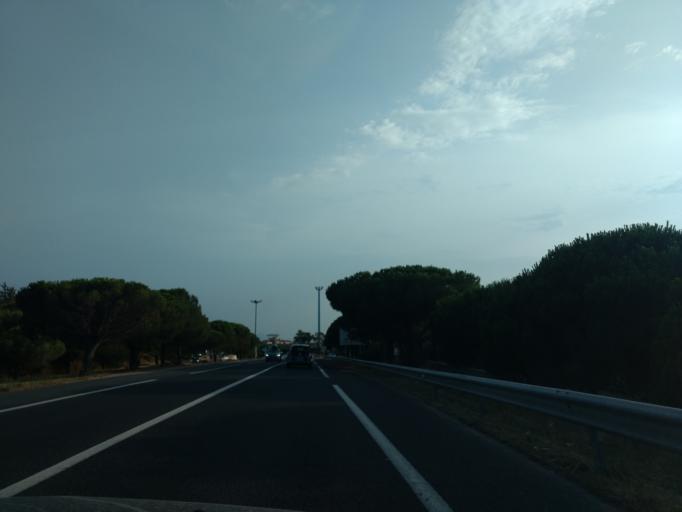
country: FR
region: Languedoc-Roussillon
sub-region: Departement des Pyrenees-Orientales
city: Canet-en-Roussillon
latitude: 42.7049
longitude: 3.0174
